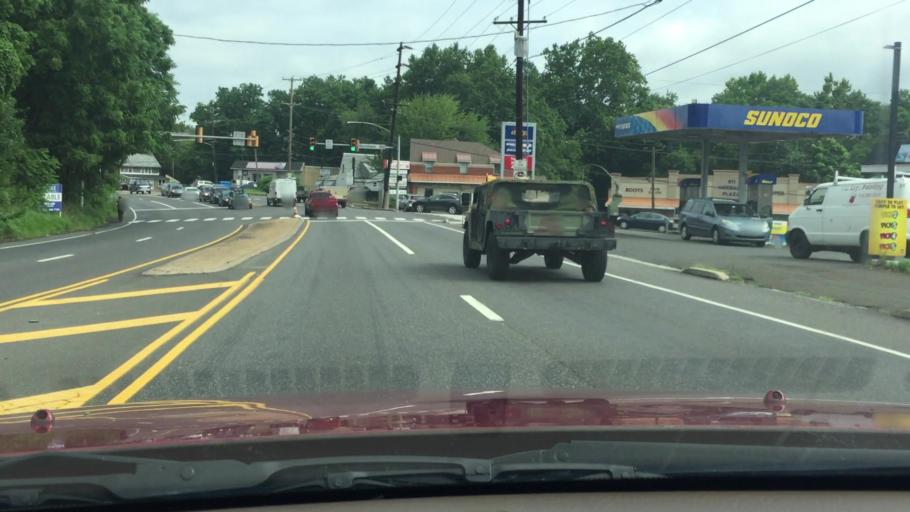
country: US
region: Pennsylvania
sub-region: Montgomery County
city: Horsham
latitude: 40.1770
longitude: -75.1282
